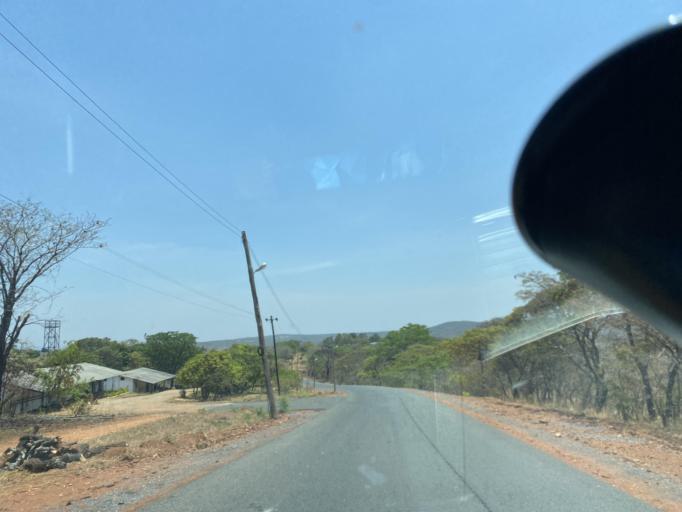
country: ZM
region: Lusaka
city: Kafue
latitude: -15.8662
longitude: 28.4507
